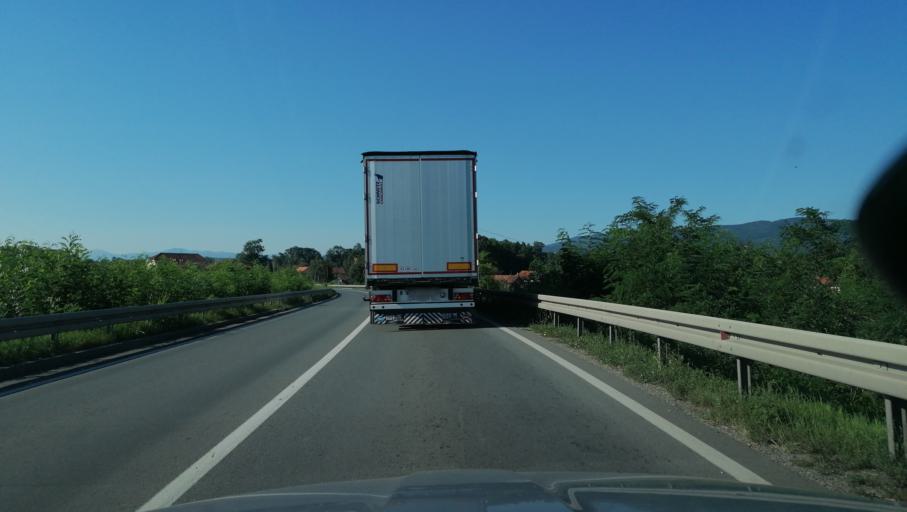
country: RS
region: Central Serbia
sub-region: Raski Okrug
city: Kraljevo
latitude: 43.7463
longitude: 20.6637
